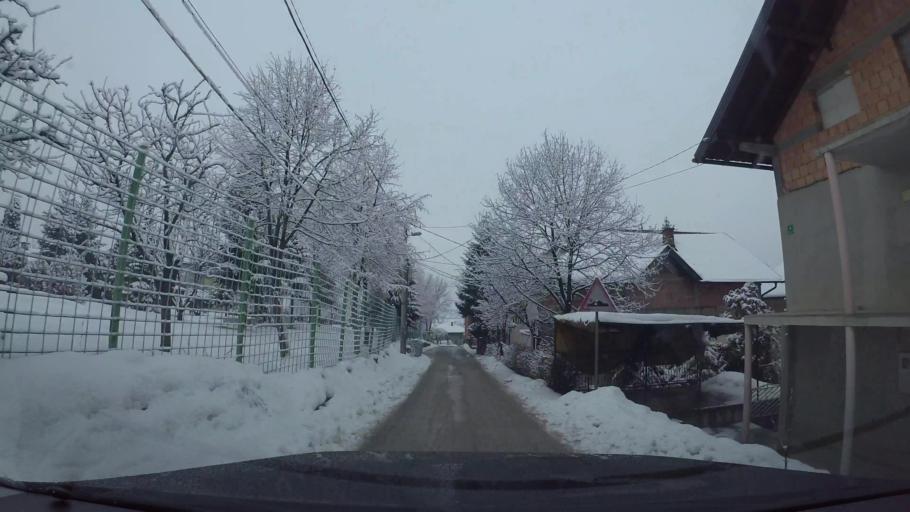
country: BA
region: Federation of Bosnia and Herzegovina
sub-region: Kanton Sarajevo
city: Sarajevo
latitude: 43.8582
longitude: 18.3230
